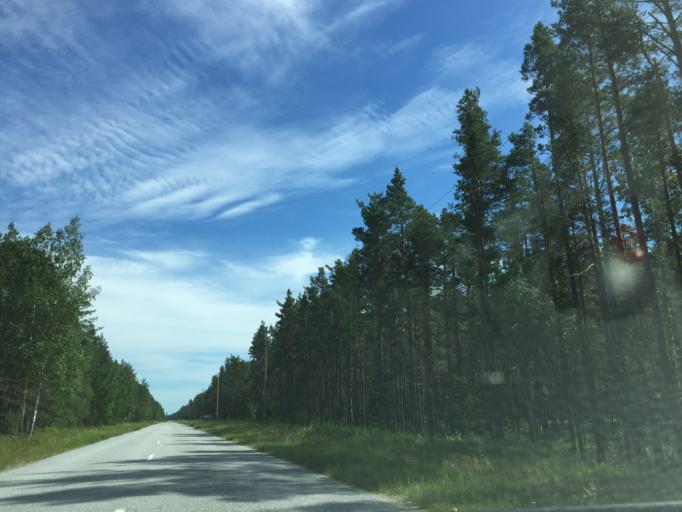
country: LV
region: Rojas
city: Roja
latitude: 57.5634
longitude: 22.6572
